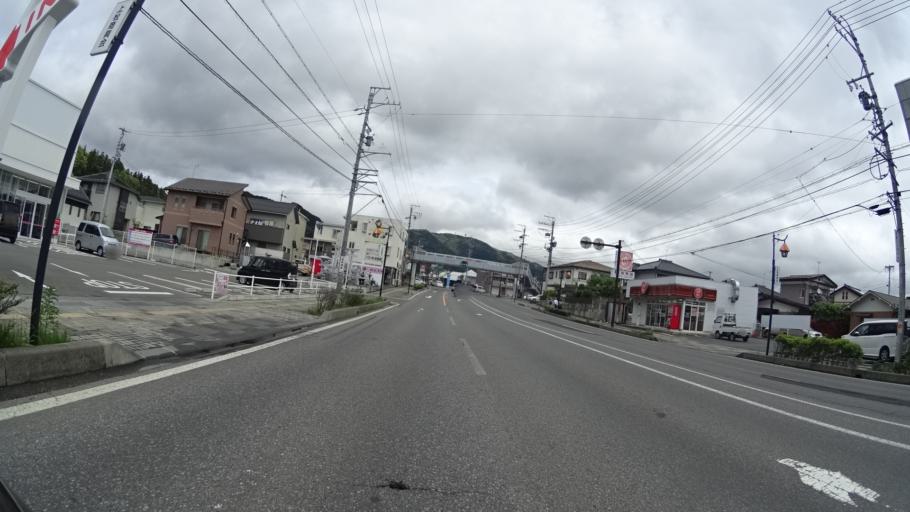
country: JP
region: Nagano
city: Nagano-shi
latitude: 36.6750
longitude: 138.1996
